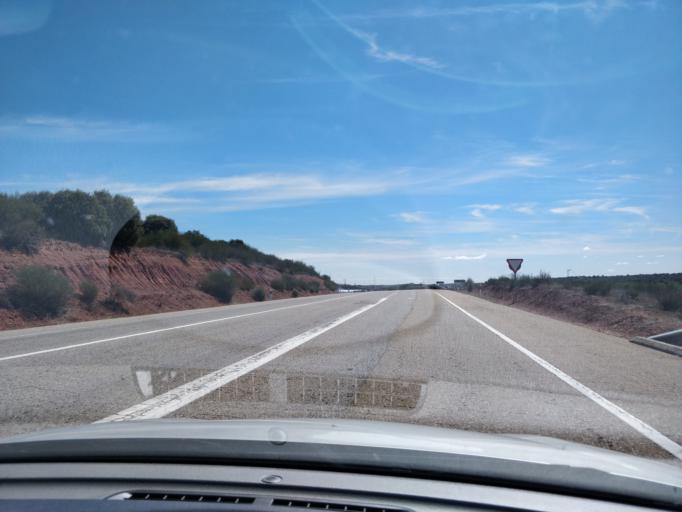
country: ES
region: Castille and Leon
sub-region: Provincia de Leon
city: Astorga
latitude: 42.4752
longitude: -6.0934
